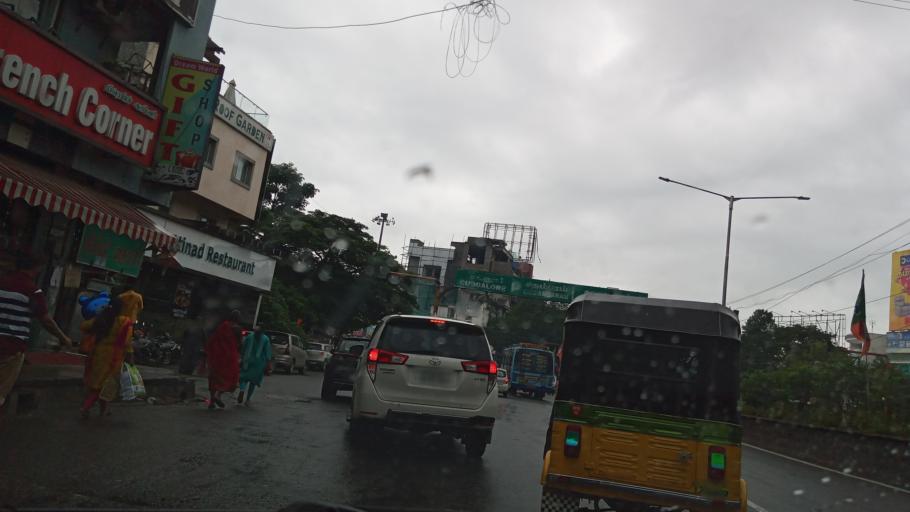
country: IN
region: Pondicherry
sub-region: Puducherry
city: Puducherry
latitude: 11.9322
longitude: 79.8076
